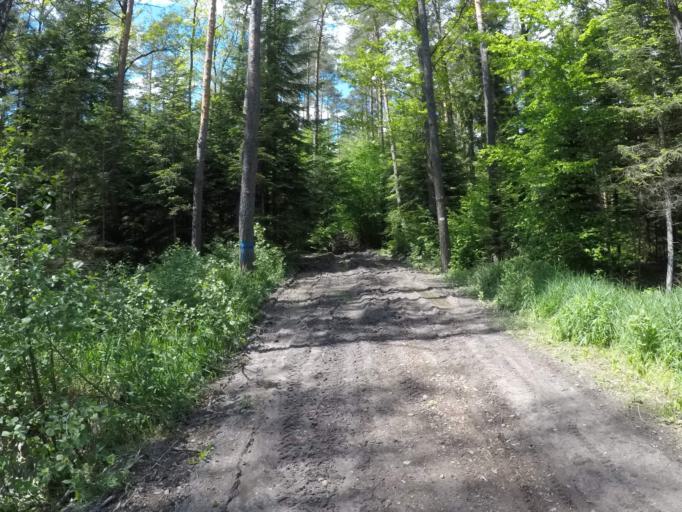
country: PL
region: Swietokrzyskie
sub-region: Powiat kielecki
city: Kostomloty Pierwsze
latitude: 50.9218
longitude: 20.6306
